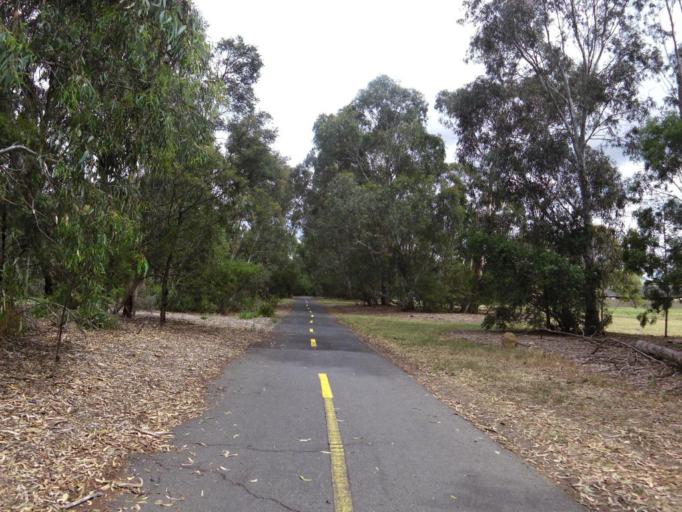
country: AU
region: Victoria
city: Heidelberg West
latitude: -37.7426
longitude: 145.0356
